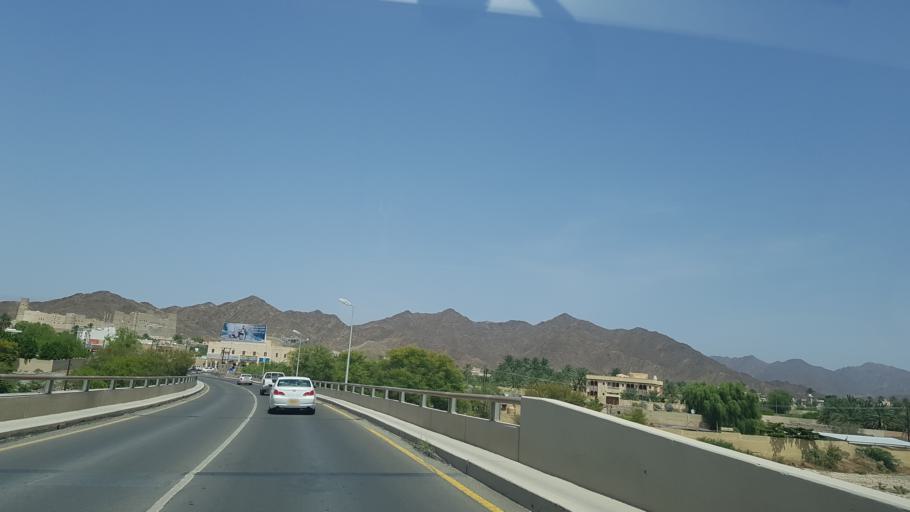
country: OM
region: Muhafazat ad Dakhiliyah
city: Bahla'
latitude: 22.9600
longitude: 57.2964
